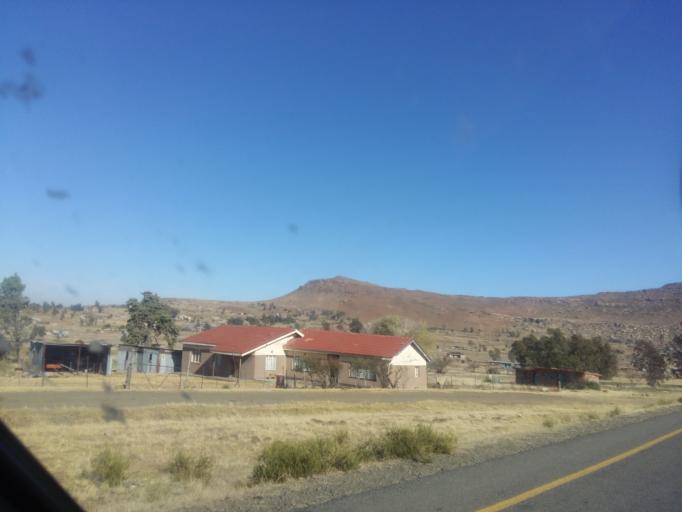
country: LS
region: Mafeteng
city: Mafeteng
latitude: -29.6954
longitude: 27.2886
